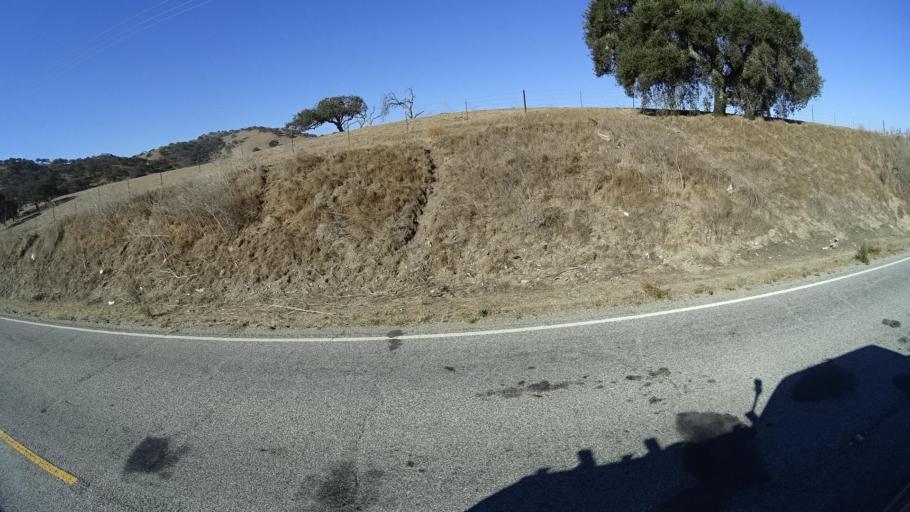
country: US
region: California
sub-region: Monterey County
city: King City
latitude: 36.1575
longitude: -121.1326
